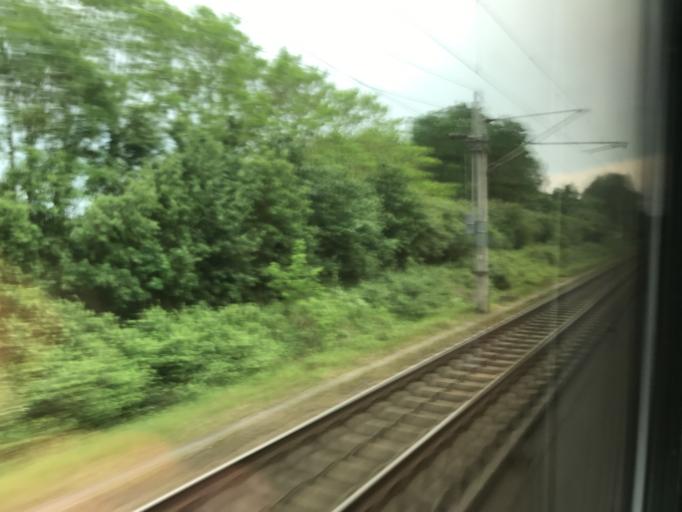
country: DE
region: Saxony-Anhalt
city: Gardelegen
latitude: 52.5116
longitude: 11.3632
